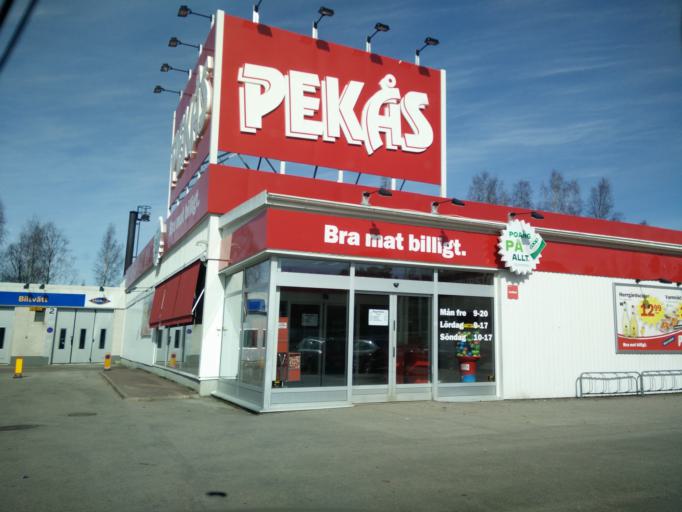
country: SE
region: Vaermland
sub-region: Hagfors Kommun
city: Hagfors
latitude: 60.0427
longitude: 13.7047
